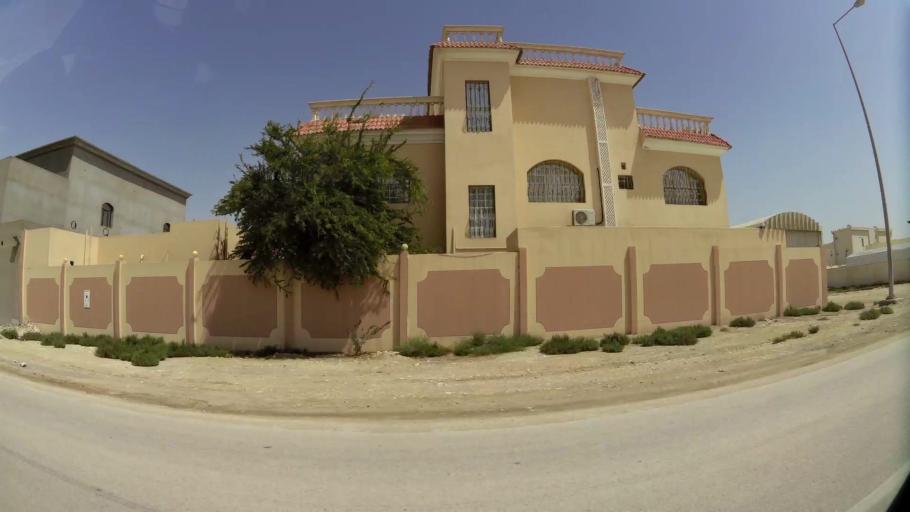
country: QA
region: Baladiyat Umm Salal
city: Umm Salal Muhammad
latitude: 25.3887
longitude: 51.4533
